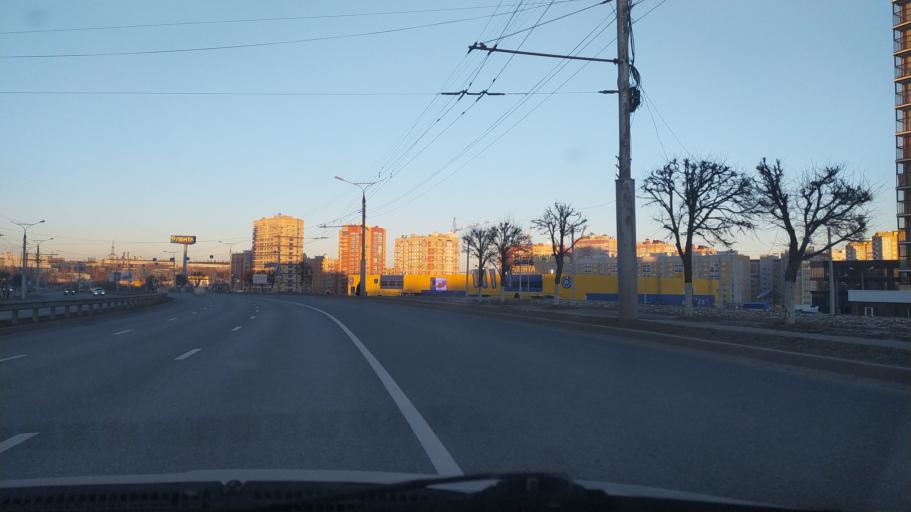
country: RU
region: Chuvashia
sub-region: Cheboksarskiy Rayon
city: Cheboksary
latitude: 56.1075
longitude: 47.3266
